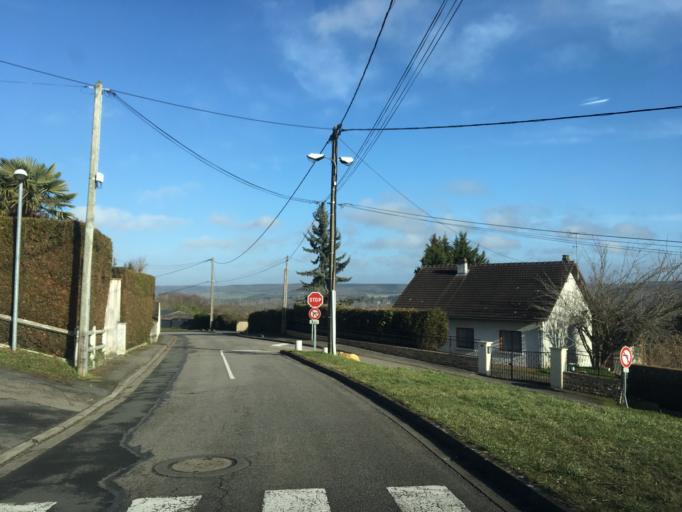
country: FR
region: Haute-Normandie
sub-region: Departement de l'Eure
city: Saint-Just
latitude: 49.1054
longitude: 1.4343
